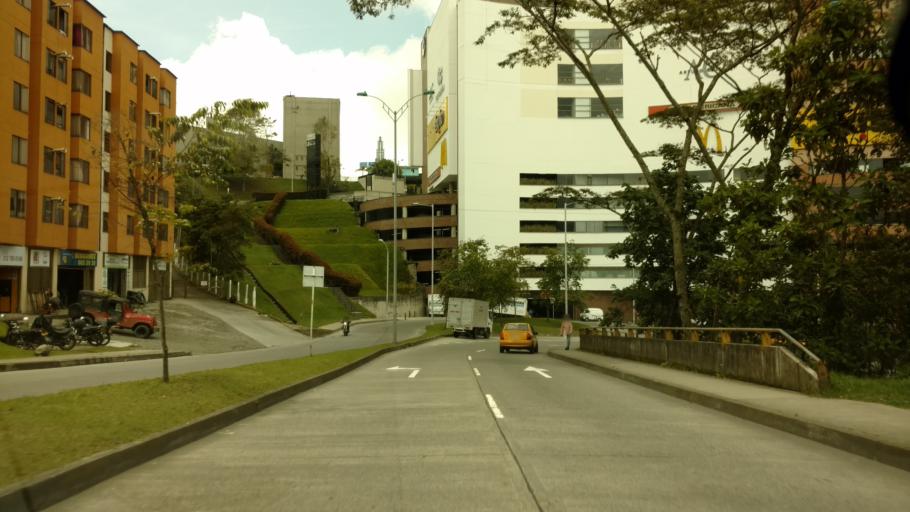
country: CO
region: Caldas
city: Manizales
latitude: 5.0688
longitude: -75.5085
